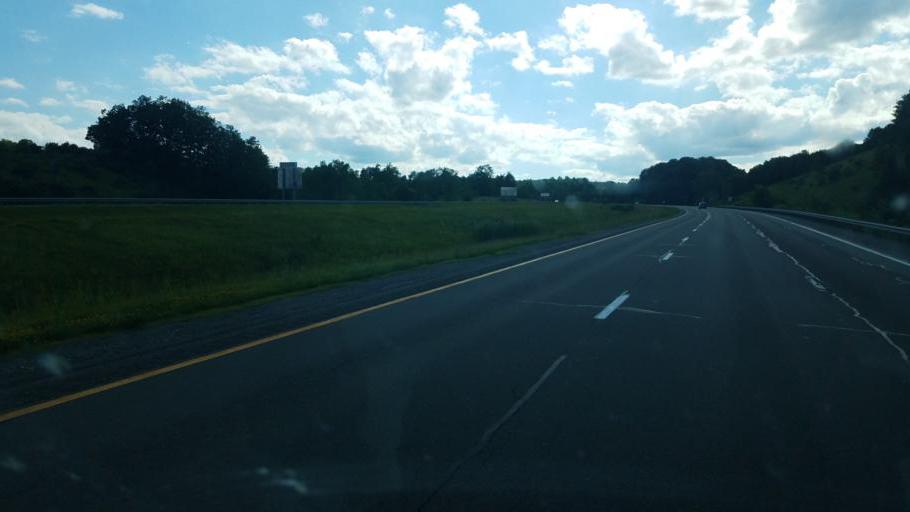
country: US
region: New York
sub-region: Steuben County
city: Hornell
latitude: 42.3672
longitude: -77.6881
